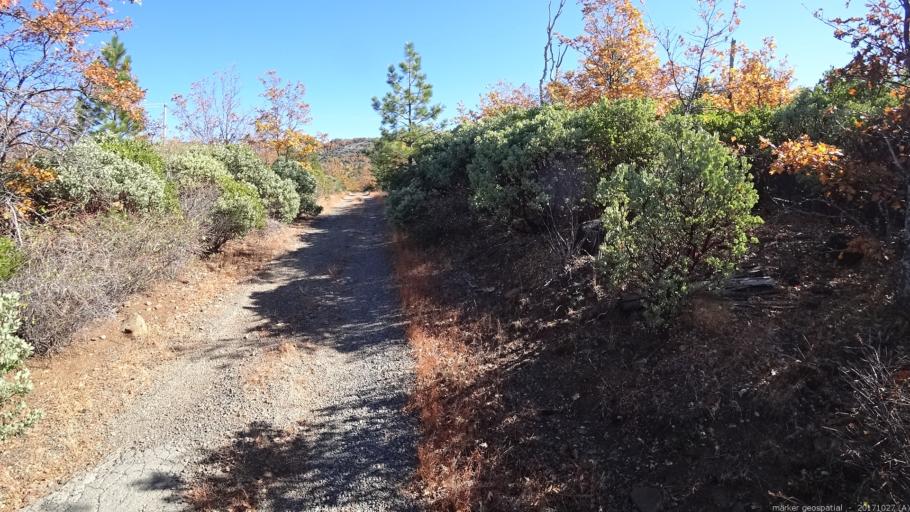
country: US
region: California
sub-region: Shasta County
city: Burney
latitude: 40.7960
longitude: -121.8965
